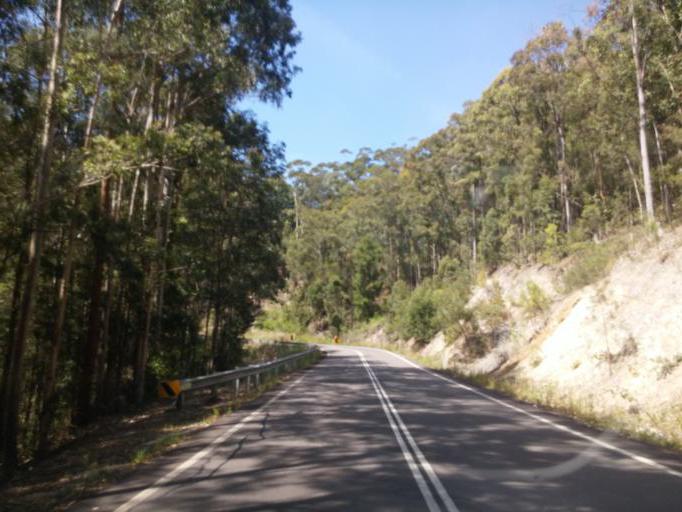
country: AU
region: New South Wales
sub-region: Great Lakes
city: Bulahdelah
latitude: -32.3937
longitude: 152.2450
